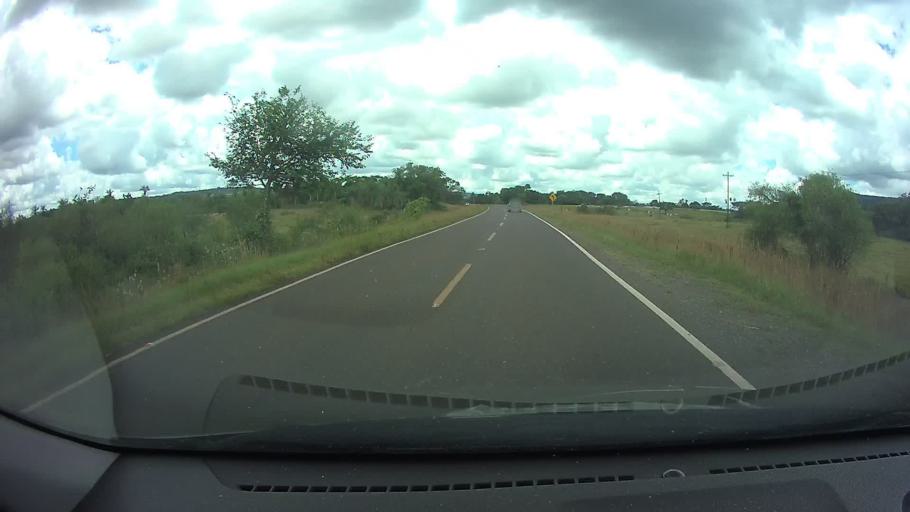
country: PY
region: Paraguari
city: Ybycui
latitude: -25.9089
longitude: -56.9843
